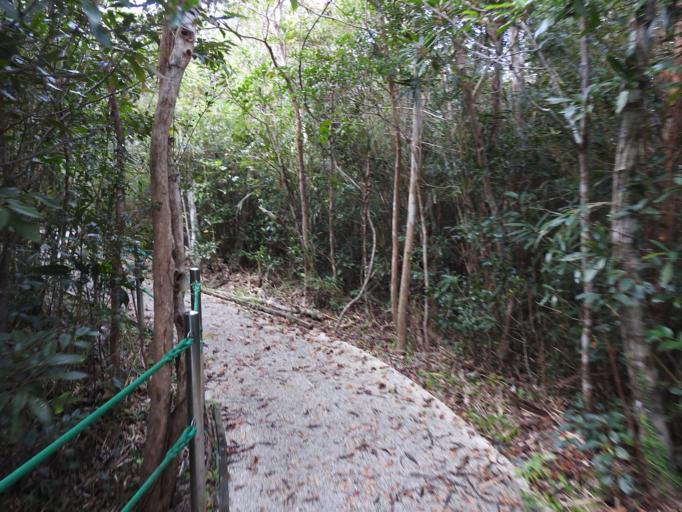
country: JP
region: Okinawa
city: Nago
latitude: 26.7210
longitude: 128.2655
